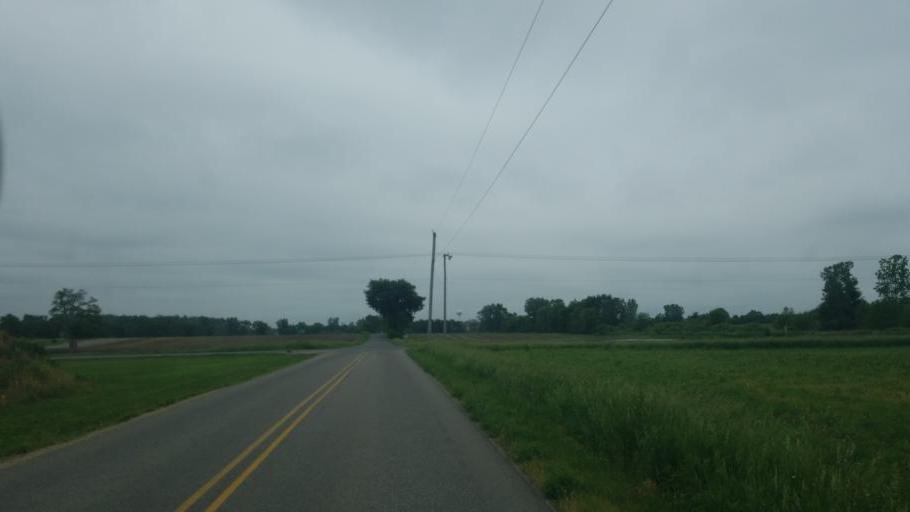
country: US
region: Indiana
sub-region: Elkhart County
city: Nappanee
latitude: 41.4580
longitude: -86.0207
